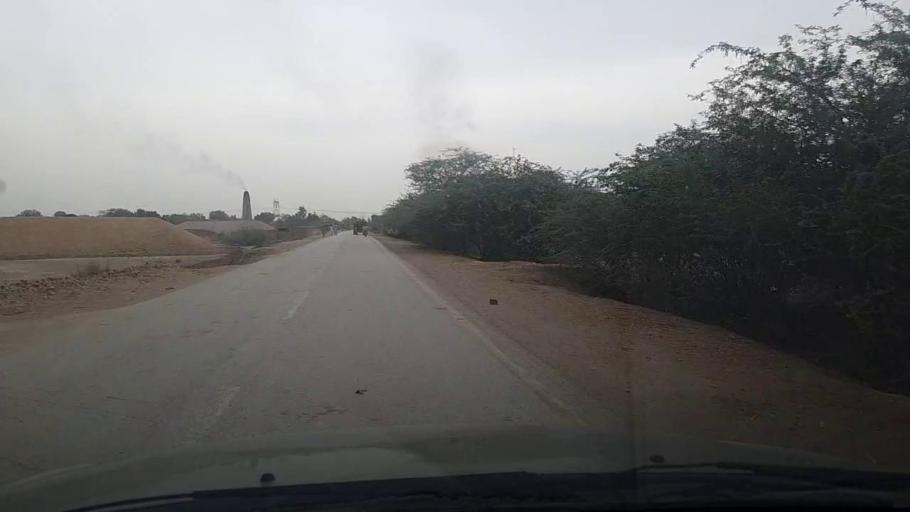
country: PK
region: Sindh
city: Daulatpur
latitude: 26.3399
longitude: 68.1226
